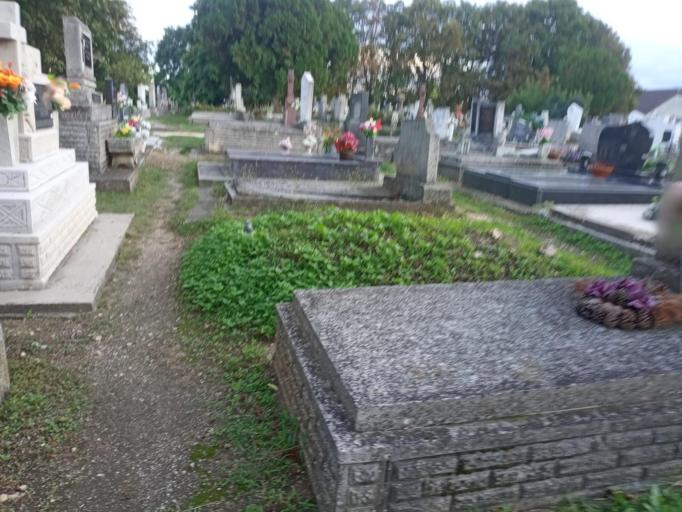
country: HU
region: Veszprem
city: Berhida
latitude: 47.1168
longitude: 18.1319
